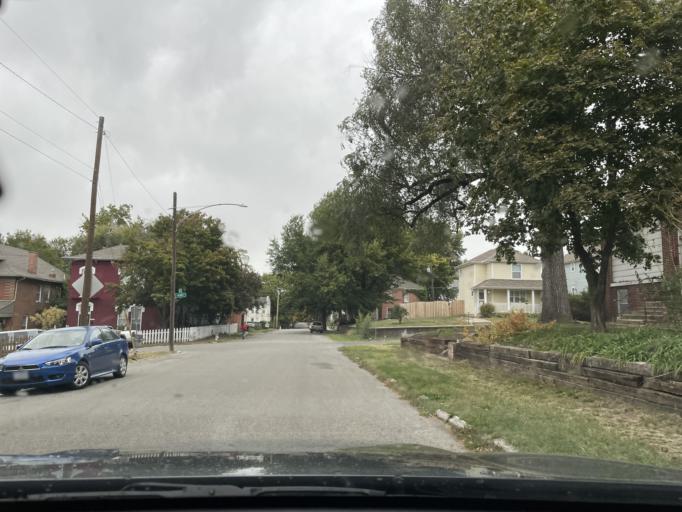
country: US
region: Missouri
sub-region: Buchanan County
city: Saint Joseph
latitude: 39.7723
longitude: -94.8467
